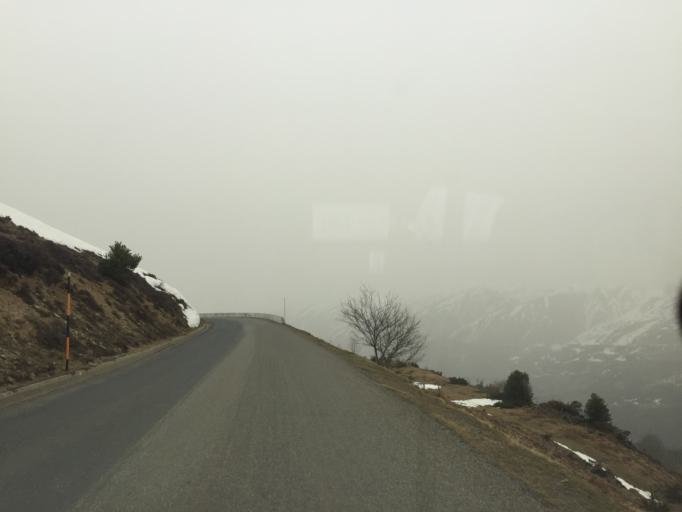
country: FR
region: Midi-Pyrenees
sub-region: Departement des Hautes-Pyrenees
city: Saint-Lary-Soulan
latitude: 42.7953
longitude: 0.3874
